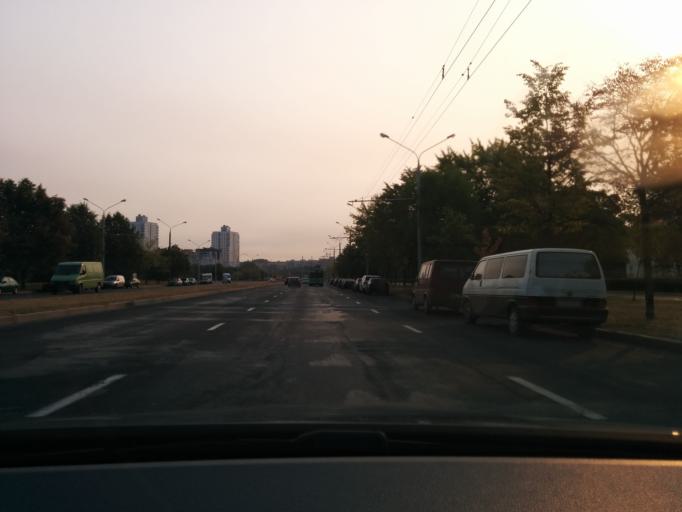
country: BY
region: Minsk
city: Minsk
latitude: 53.8536
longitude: 27.6189
